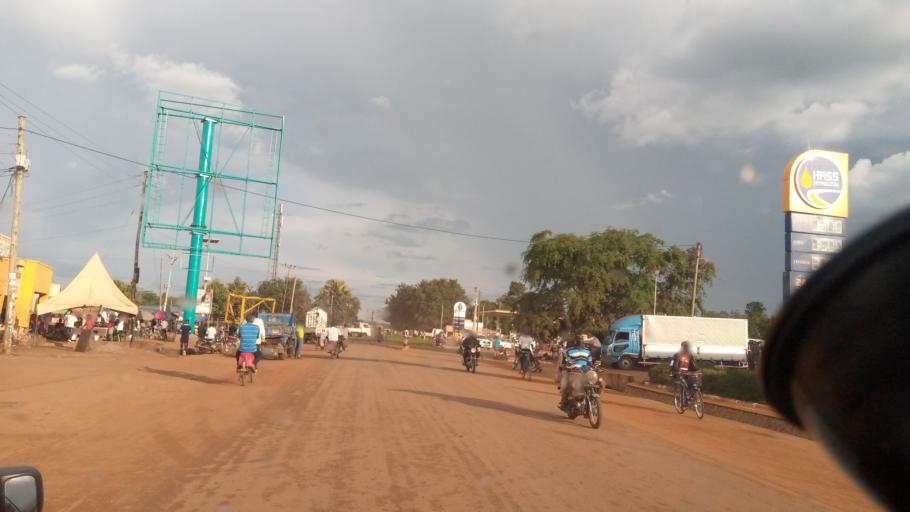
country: UG
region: Northern Region
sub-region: Lira District
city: Lira
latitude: 2.2364
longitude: 32.8914
